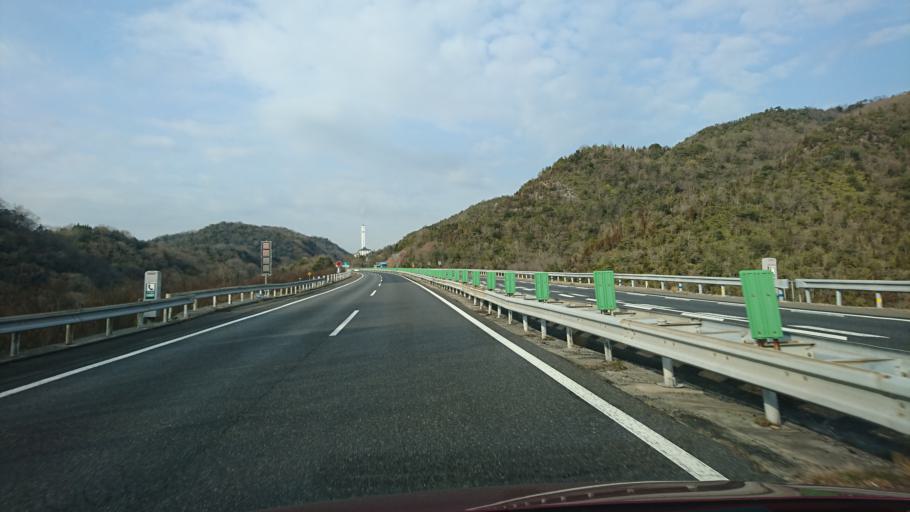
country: JP
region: Hyogo
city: Kariya
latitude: 34.7789
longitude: 134.2441
